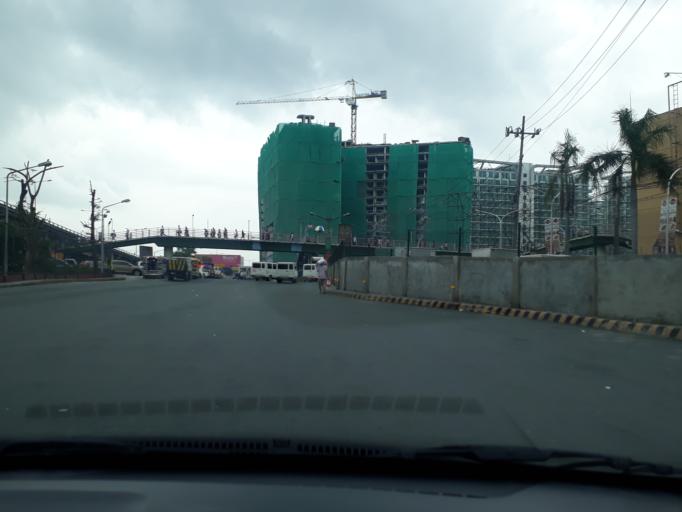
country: PH
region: Calabarzon
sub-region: Province of Rizal
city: Taguig
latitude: 14.4876
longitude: 121.0444
